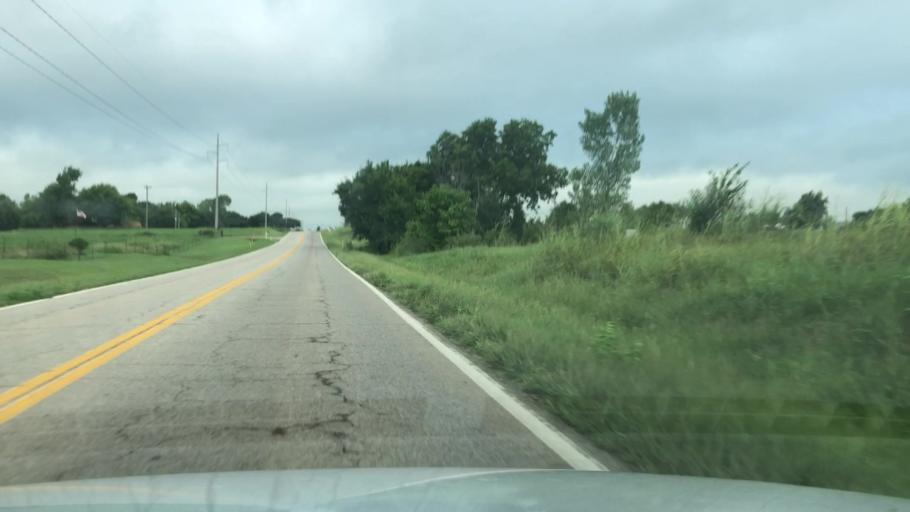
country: US
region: Oklahoma
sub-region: Nowata County
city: Nowata
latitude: 36.7136
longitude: -95.6806
